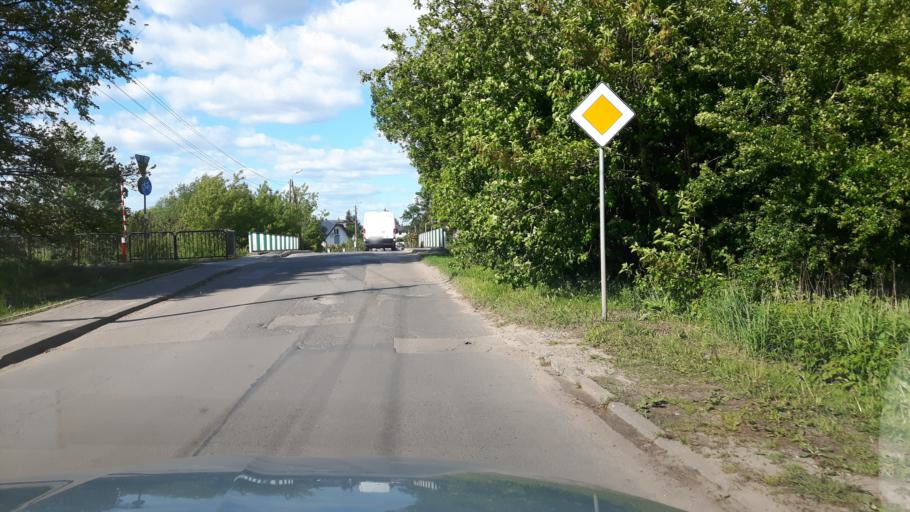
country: PL
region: Masovian Voivodeship
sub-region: Powiat wolominski
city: Marki
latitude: 52.3191
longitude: 21.1159
